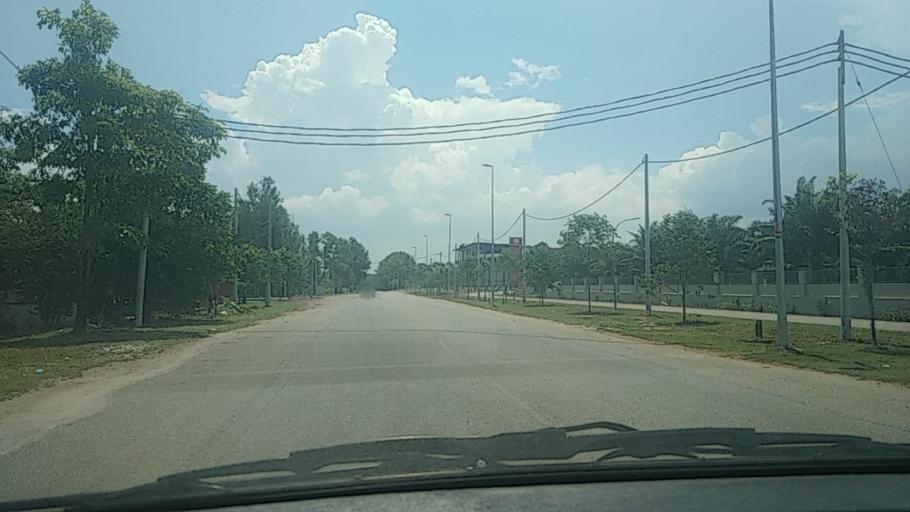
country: MY
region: Kedah
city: Sungai Petani
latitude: 5.6580
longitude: 100.5314
